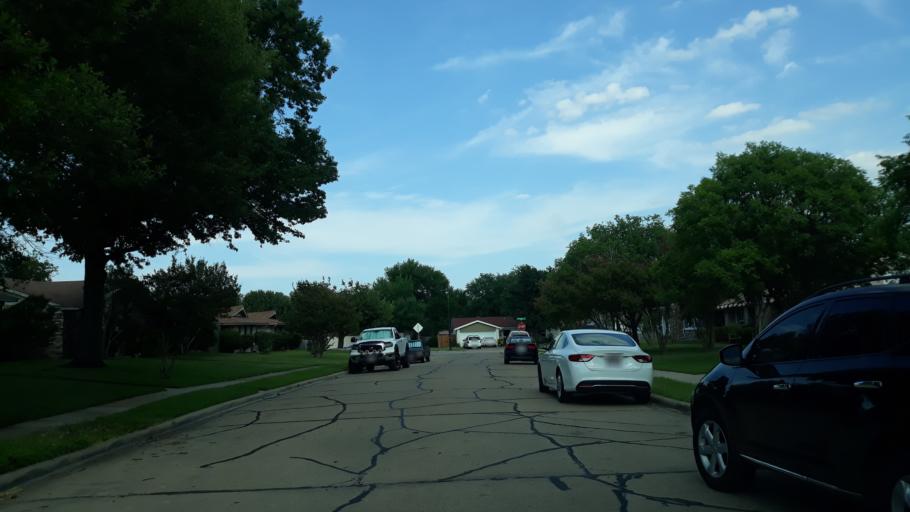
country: US
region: Texas
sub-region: Dallas County
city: Irving
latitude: 32.8492
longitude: -97.0017
